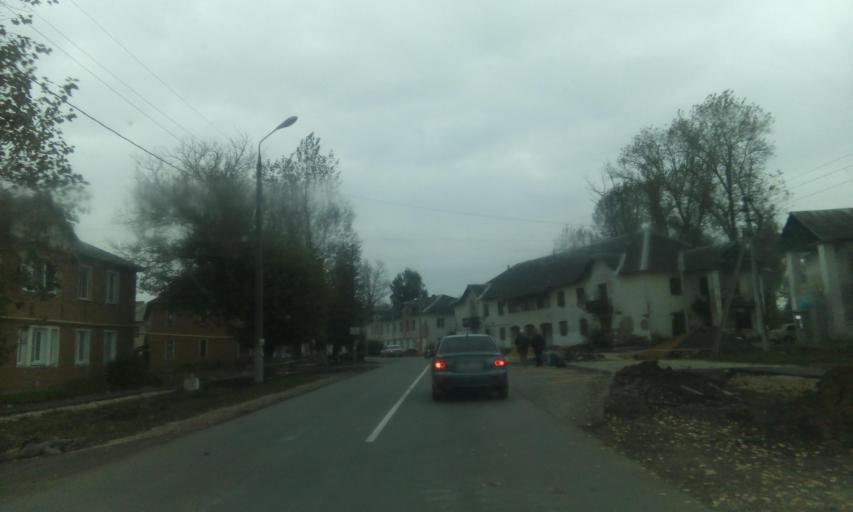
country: RU
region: Tula
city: Partizan
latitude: 53.9495
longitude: 38.0976
